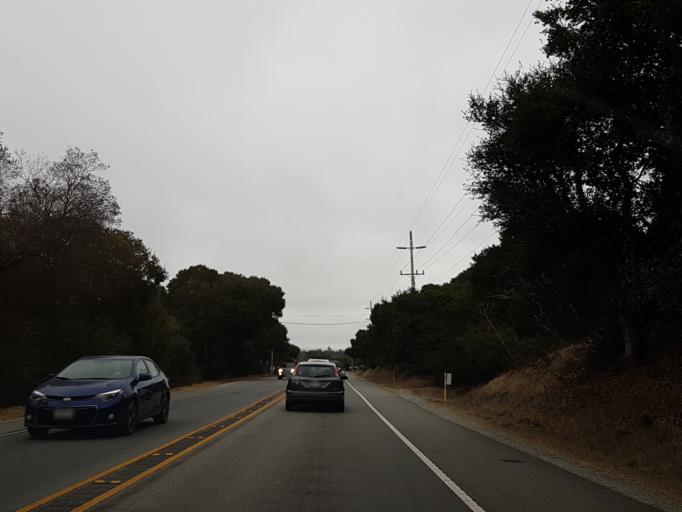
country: US
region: California
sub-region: Monterey County
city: Carmel Valley Village
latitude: 36.5705
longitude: -121.7649
